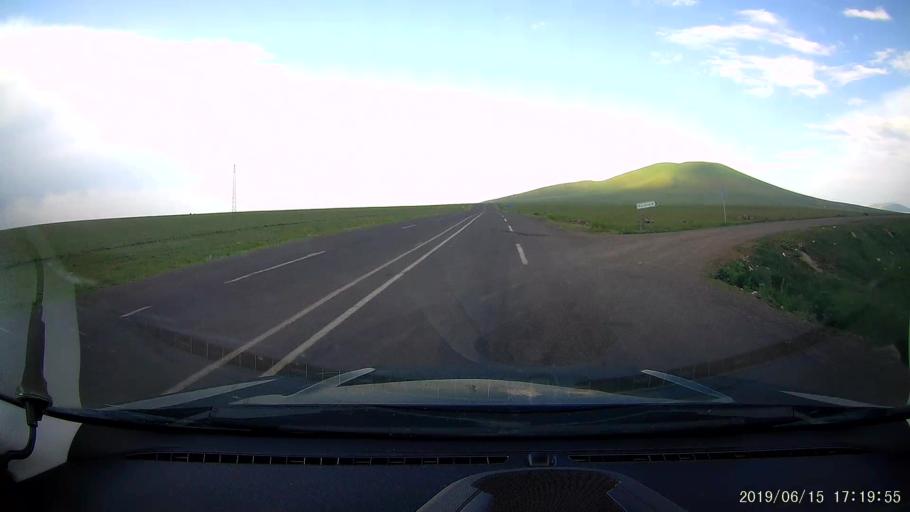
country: TR
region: Kars
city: Kars
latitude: 40.6159
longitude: 43.2893
